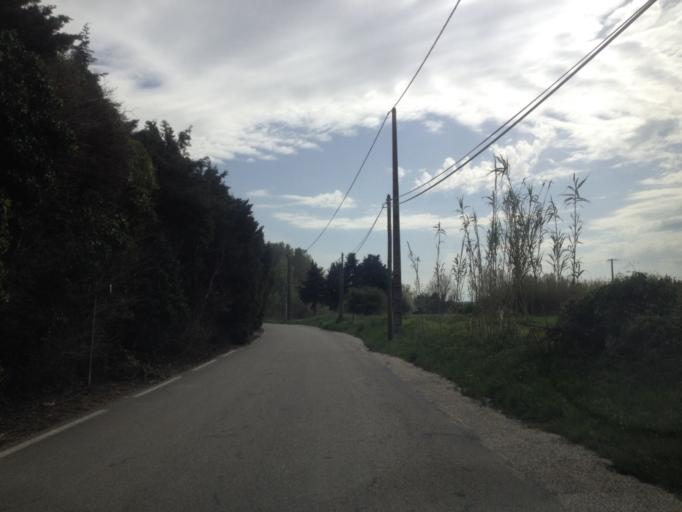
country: FR
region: Provence-Alpes-Cote d'Azur
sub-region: Departement du Vaucluse
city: Orange
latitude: 44.1224
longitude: 4.7815
